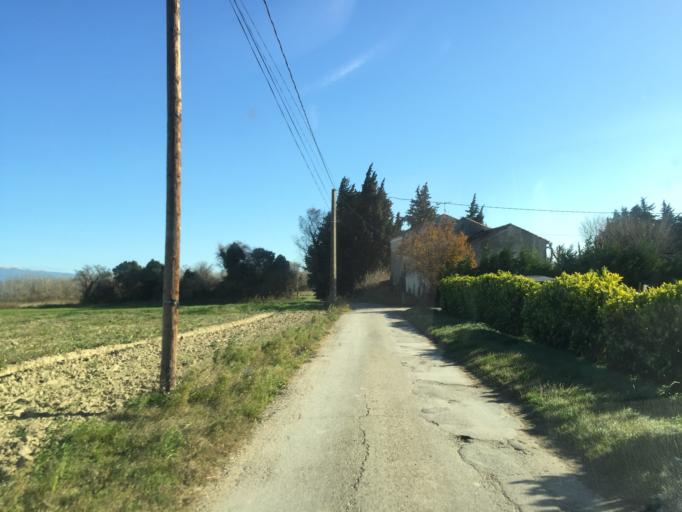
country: FR
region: Provence-Alpes-Cote d'Azur
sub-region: Departement du Vaucluse
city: Courthezon
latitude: 44.0760
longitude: 4.9236
